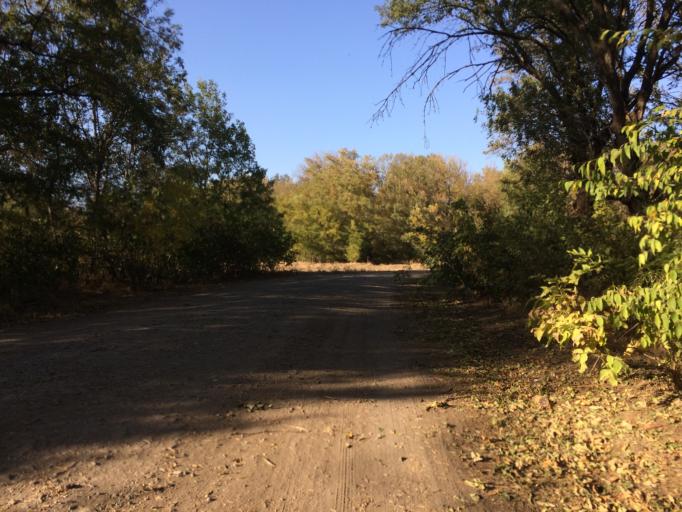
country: RU
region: Rostov
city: Tselina
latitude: 46.5156
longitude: 41.1828
